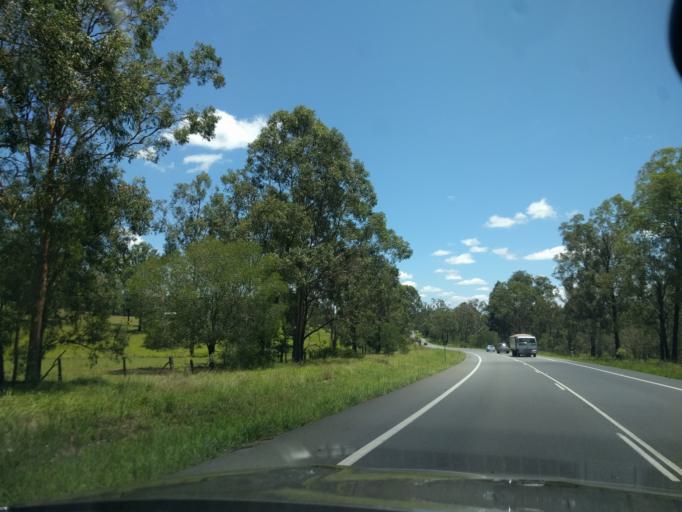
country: AU
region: Queensland
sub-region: Logan
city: Cedar Vale
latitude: -27.8699
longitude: 152.9984
